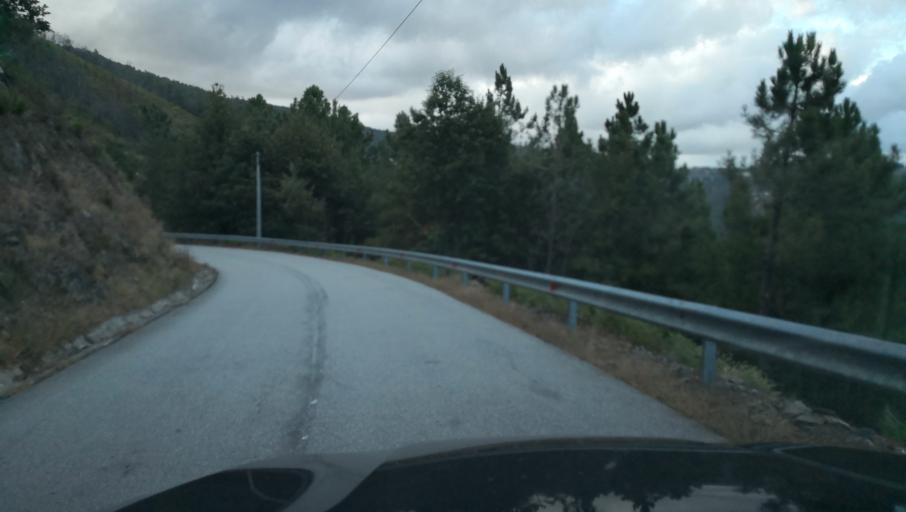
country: PT
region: Vila Real
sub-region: Santa Marta de Penaguiao
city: Santa Marta de Penaguiao
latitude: 41.2537
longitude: -7.8538
